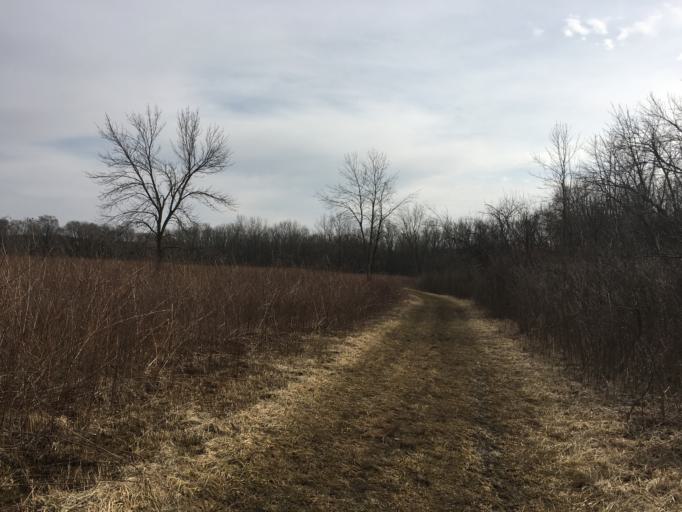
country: US
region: Illinois
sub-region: Cook County
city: Streamwood
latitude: 42.0517
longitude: -88.2085
